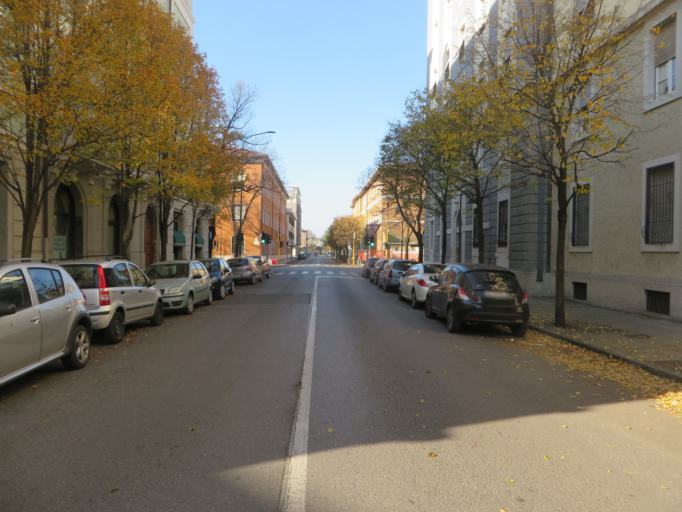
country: IT
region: Lombardy
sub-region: Provincia di Brescia
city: Brescia
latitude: 45.5493
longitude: 10.2153
